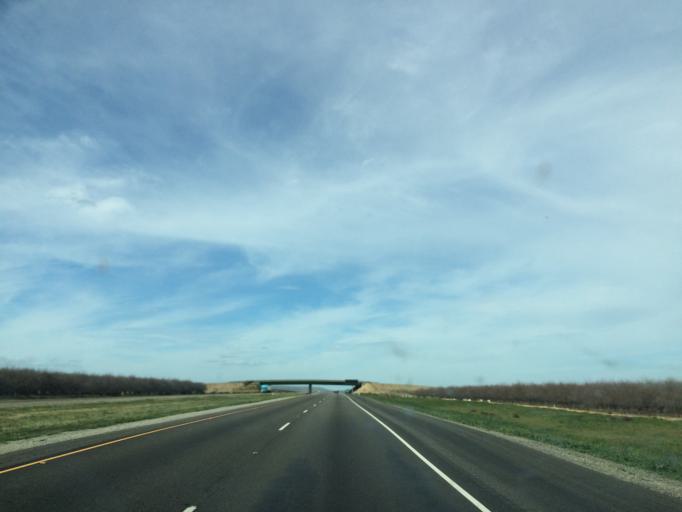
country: US
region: California
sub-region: Merced County
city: South Dos Palos
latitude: 36.7573
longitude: -120.7096
